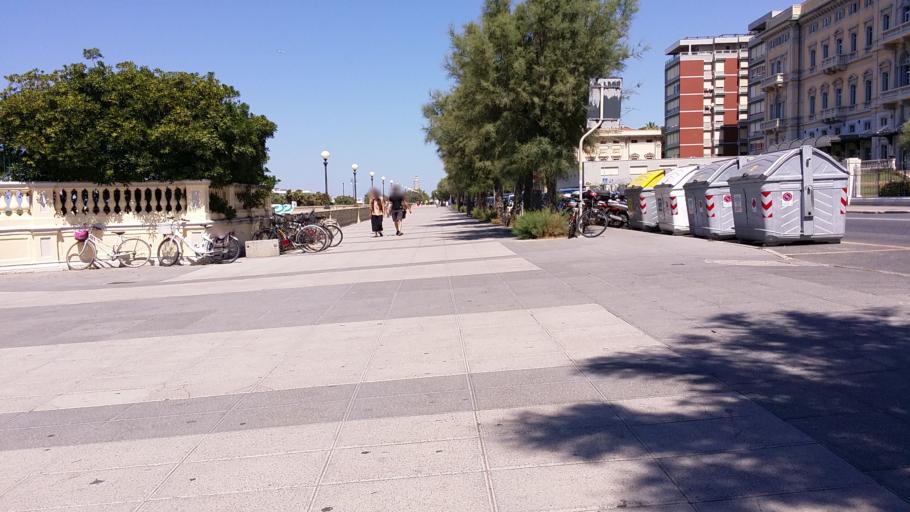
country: IT
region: Tuscany
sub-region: Provincia di Livorno
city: Livorno
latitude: 43.5320
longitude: 10.3026
